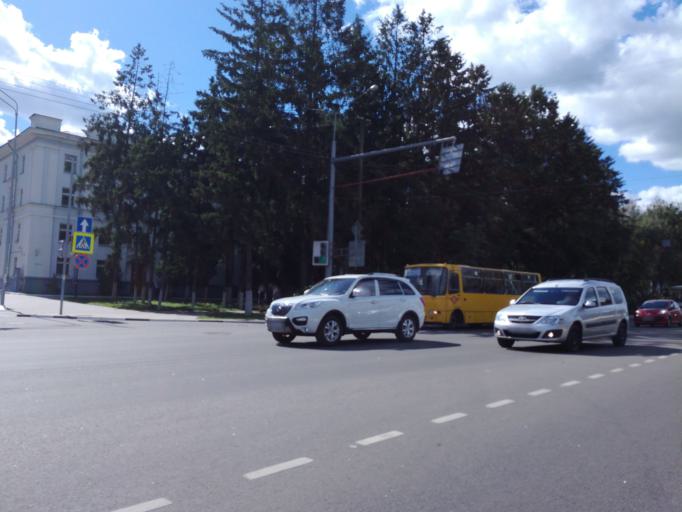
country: RU
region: Kursk
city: Kursk
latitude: 51.7633
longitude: 36.1844
